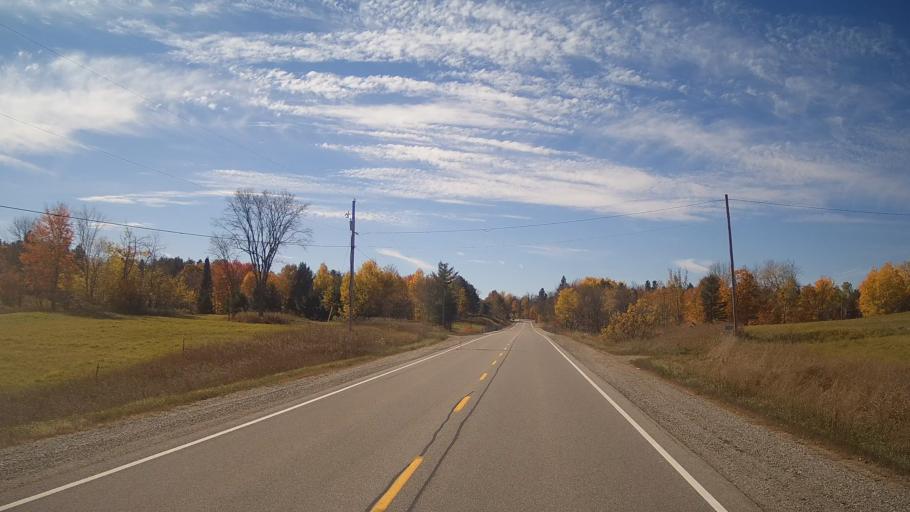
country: CA
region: Ontario
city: Perth
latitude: 44.8158
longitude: -76.6283
